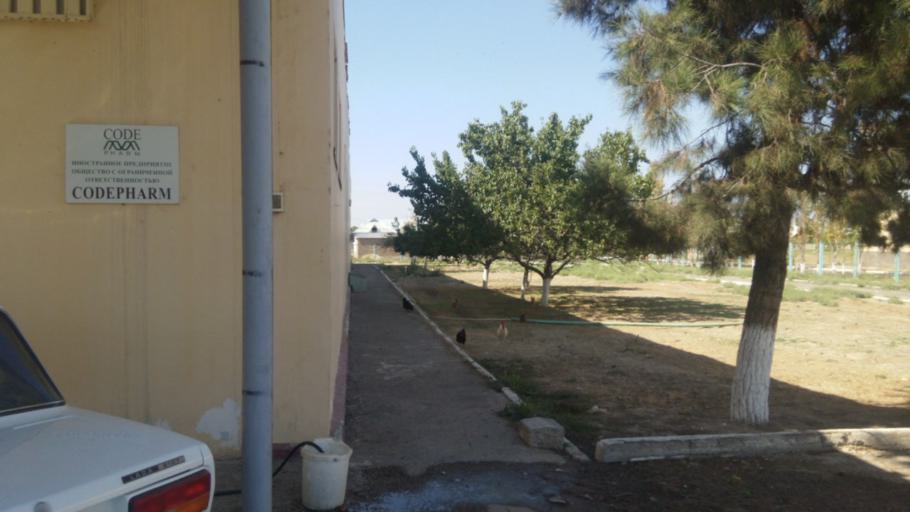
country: UZ
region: Sirdaryo
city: Guliston
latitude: 40.5152
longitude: 68.7857
